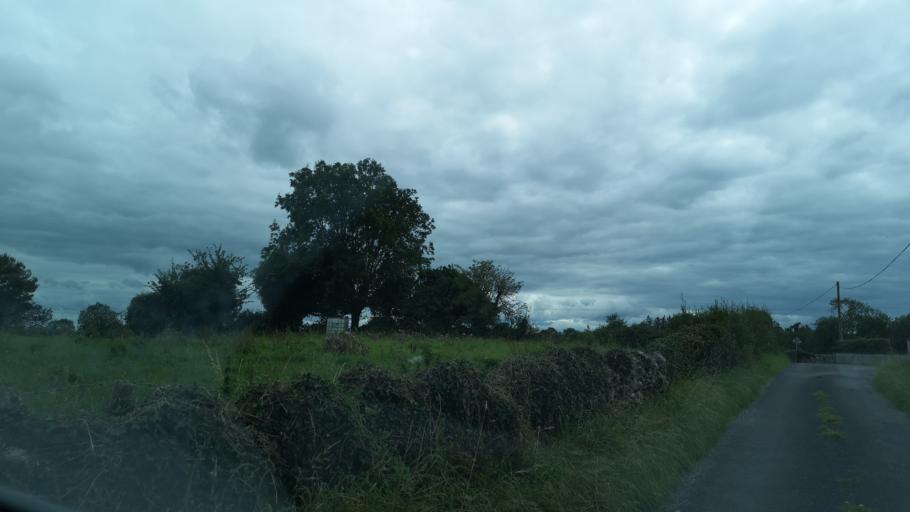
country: IE
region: Connaught
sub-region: County Galway
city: Loughrea
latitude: 53.1621
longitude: -8.4703
